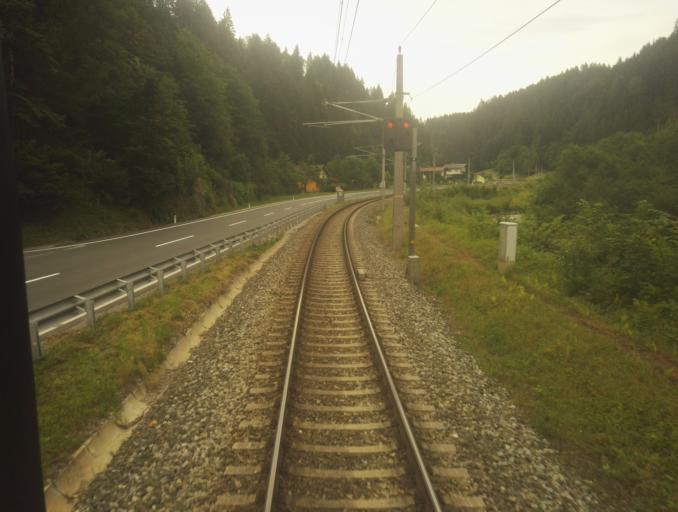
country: AT
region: Salzburg
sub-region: Politischer Bezirk Sankt Johann im Pongau
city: Bischofshofen
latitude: 47.4321
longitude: 13.2385
